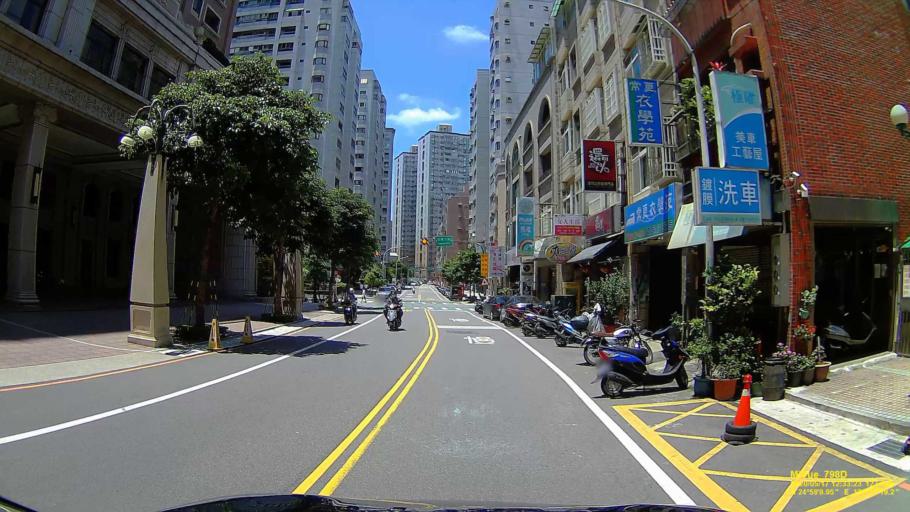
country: TW
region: Taiwan
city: Taoyuan City
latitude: 24.9862
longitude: 121.2886
